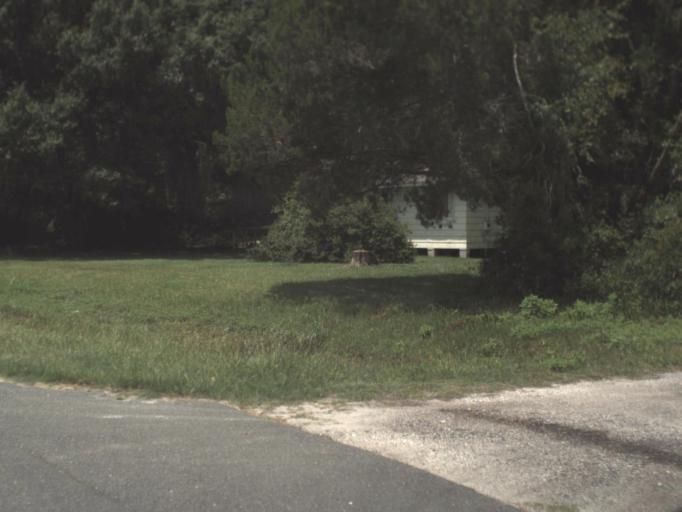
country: US
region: Florida
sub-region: Alachua County
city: Alachua
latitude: 29.8610
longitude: -82.3449
